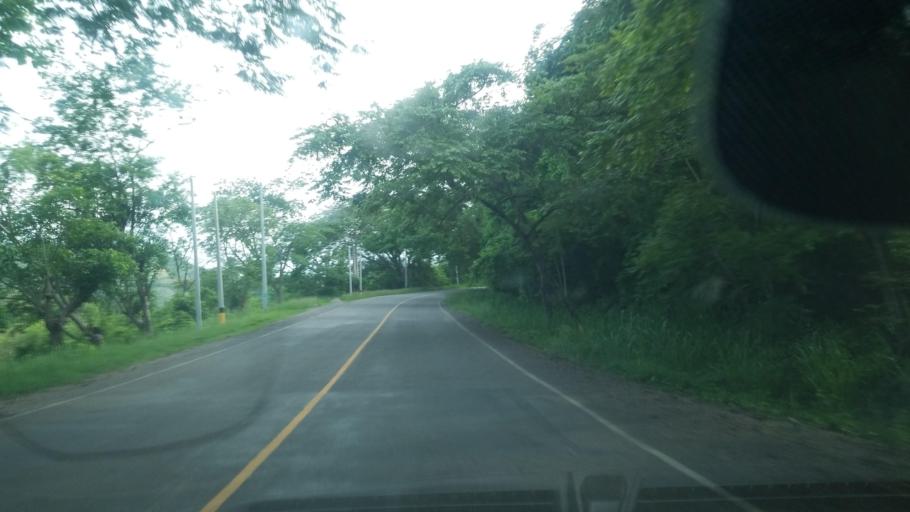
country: HN
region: Santa Barbara
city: Ilama
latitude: 15.1015
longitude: -88.2004
